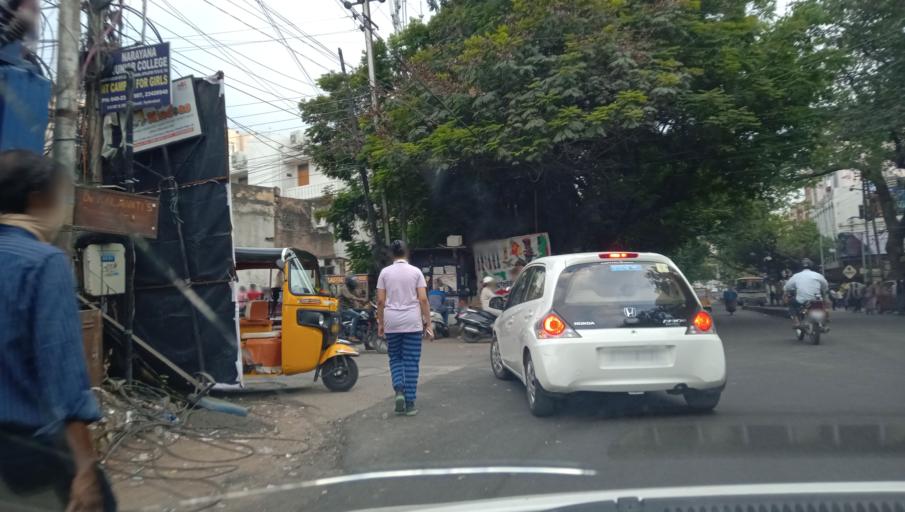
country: IN
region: Telangana
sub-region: Hyderabad
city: Hyderabad
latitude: 17.3992
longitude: 78.4861
